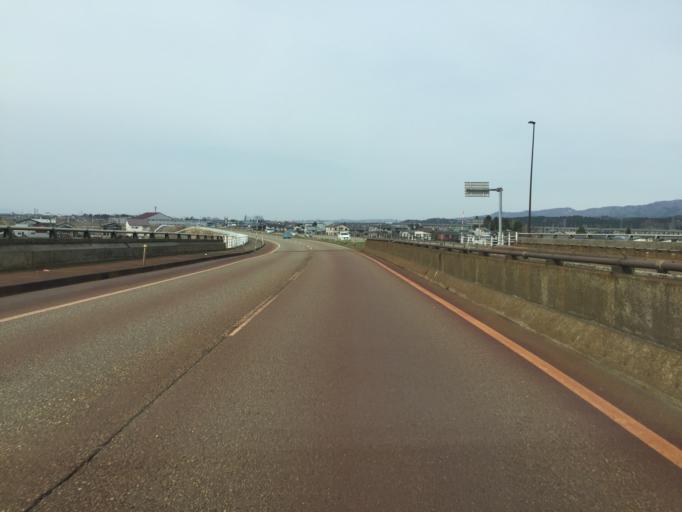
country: JP
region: Niigata
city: Nagaoka
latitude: 37.3888
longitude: 138.8354
